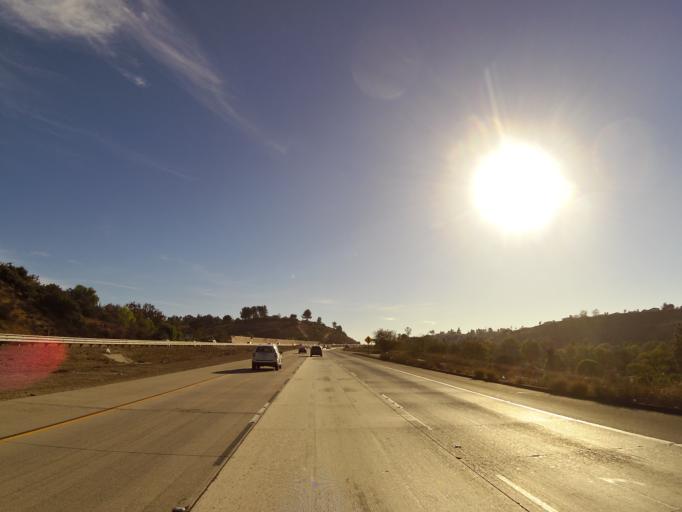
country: US
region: California
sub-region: Ventura County
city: Moorpark
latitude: 34.2386
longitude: -118.8411
